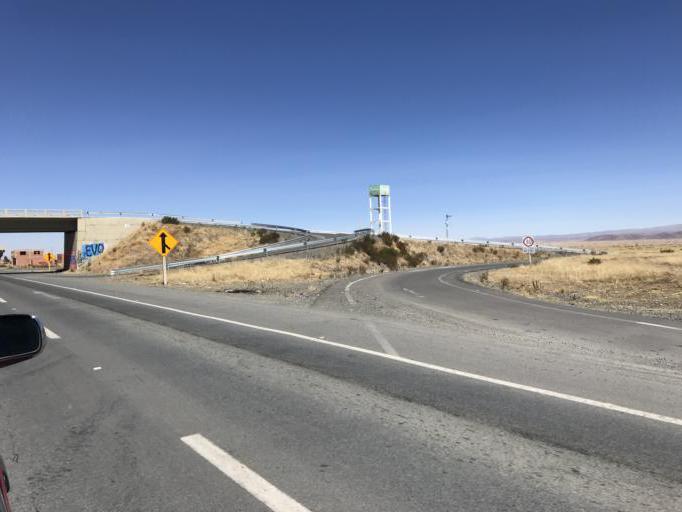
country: BO
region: La Paz
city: Batallas
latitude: -16.3687
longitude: -68.3875
